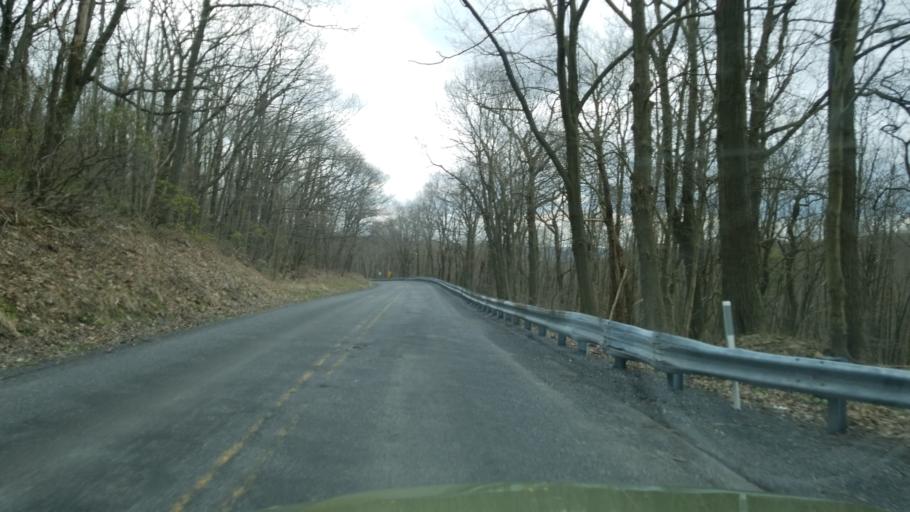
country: US
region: Pennsylvania
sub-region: Blair County
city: Tipton
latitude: 40.7217
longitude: -78.3525
